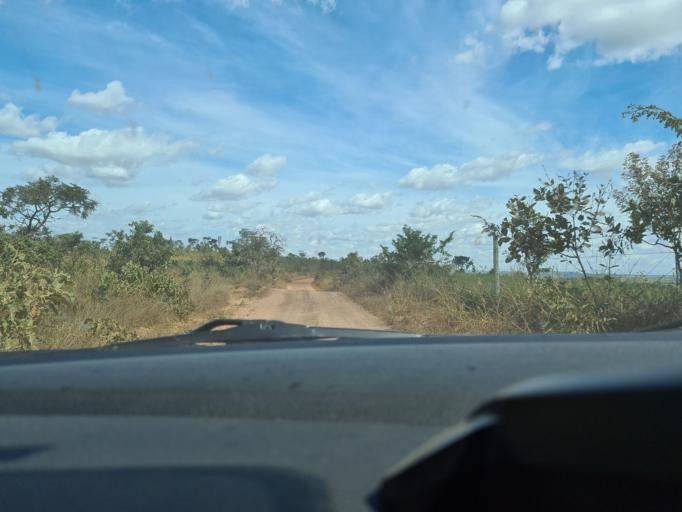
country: BR
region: Goias
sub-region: Silvania
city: Silvania
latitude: -16.5407
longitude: -48.5677
